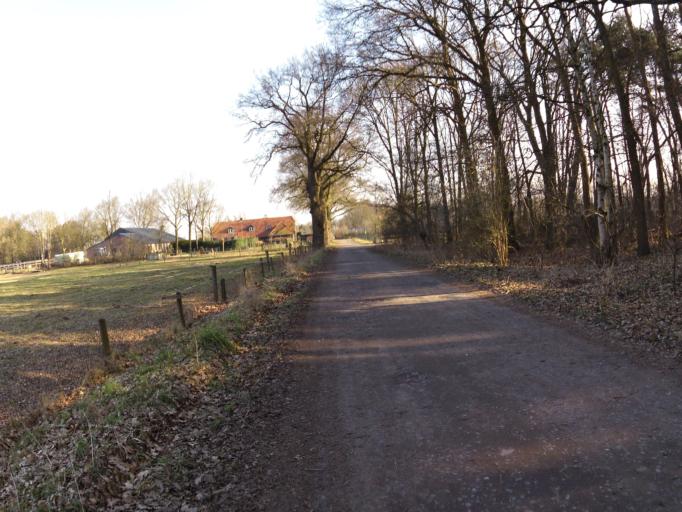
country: NL
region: North Brabant
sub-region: Gemeente Maasdonk
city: Geffen
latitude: 51.7182
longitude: 5.4241
